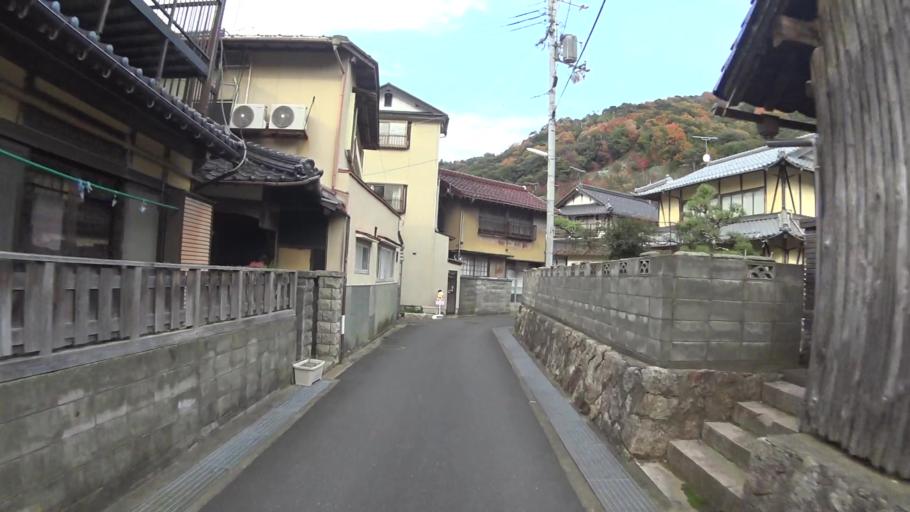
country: JP
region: Kyoto
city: Maizuru
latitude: 35.5696
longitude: 135.4287
